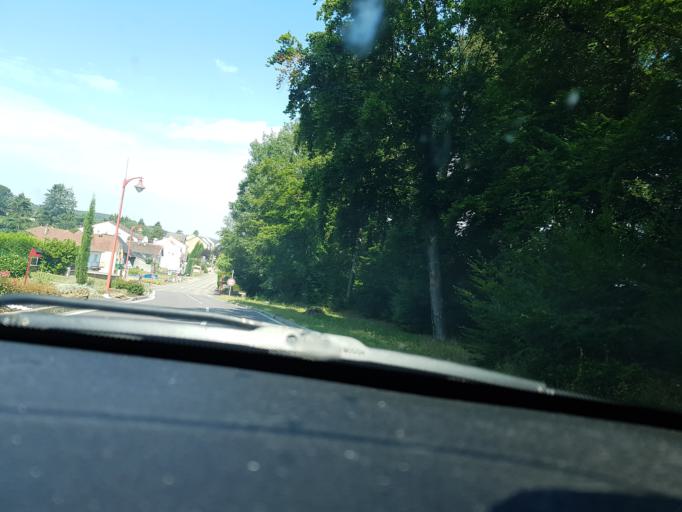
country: FR
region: Lorraine
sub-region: Departement de la Moselle
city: Porcelette
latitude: 49.1511
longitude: 6.6659
